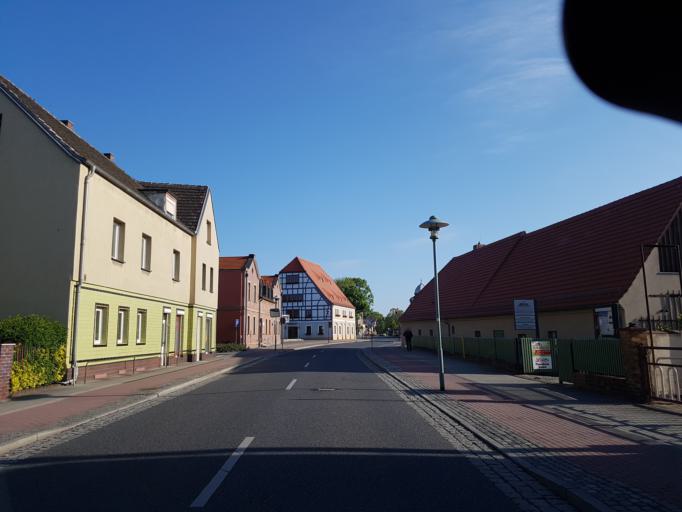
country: DE
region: Brandenburg
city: Grossraschen
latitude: 51.5867
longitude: 14.0107
